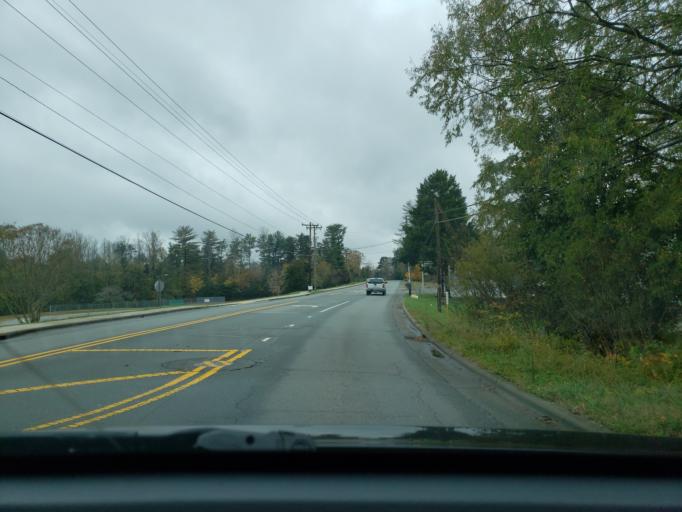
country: US
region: North Carolina
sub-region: Stokes County
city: Walnut Cove
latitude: 36.3102
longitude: -80.1400
